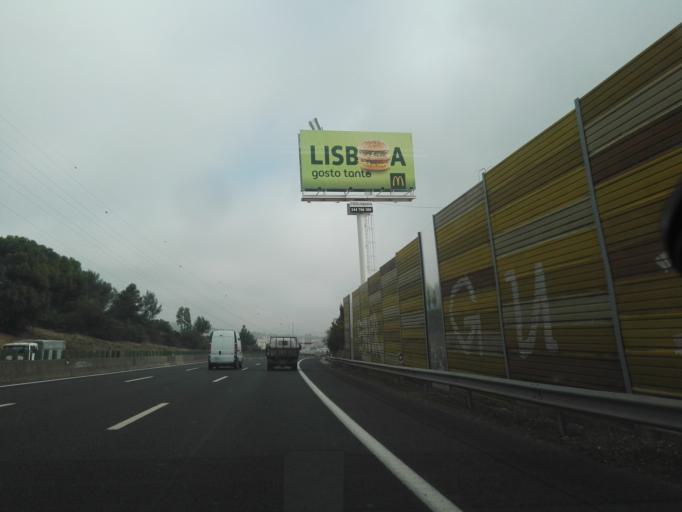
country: PT
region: Lisbon
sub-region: Vila Franca de Xira
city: Vialonga
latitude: 38.8639
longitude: -9.0800
